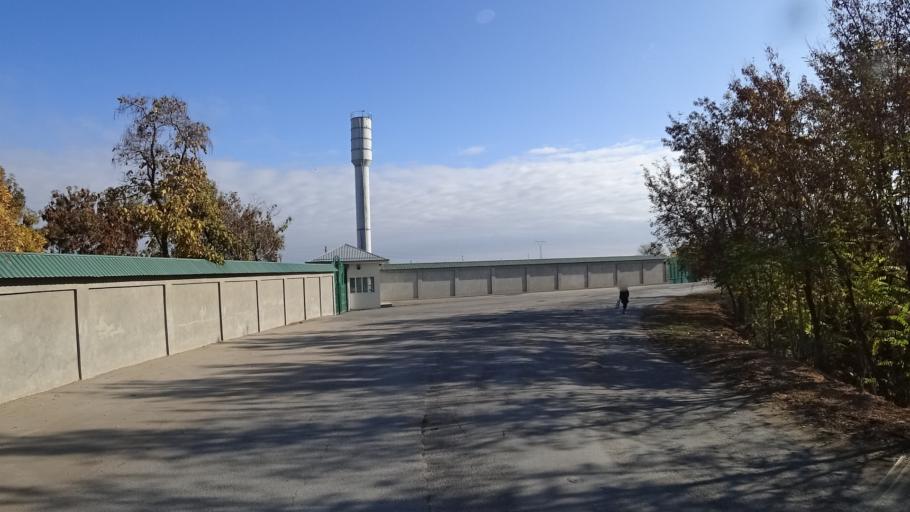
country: UZ
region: Sirdaryo
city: Sirdaryo
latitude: 40.9041
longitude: 68.6903
